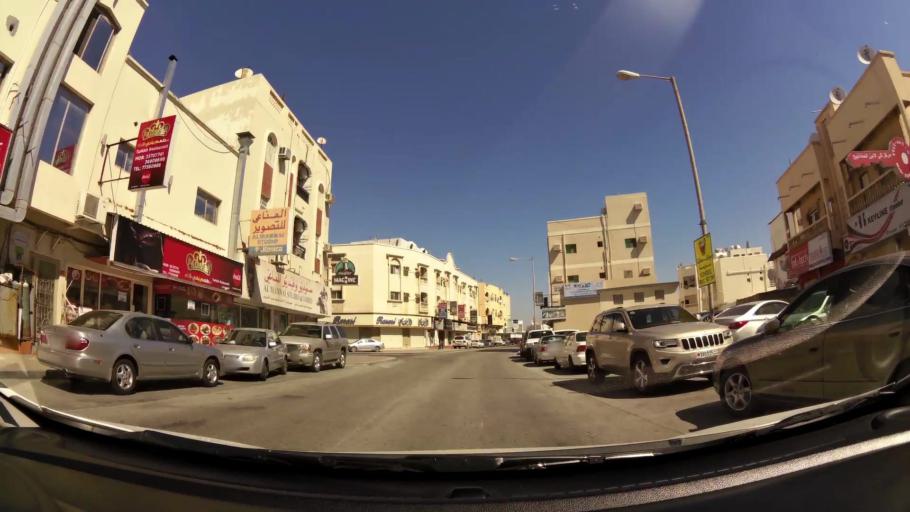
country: BH
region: Muharraq
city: Al Muharraq
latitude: 26.2527
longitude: 50.6193
